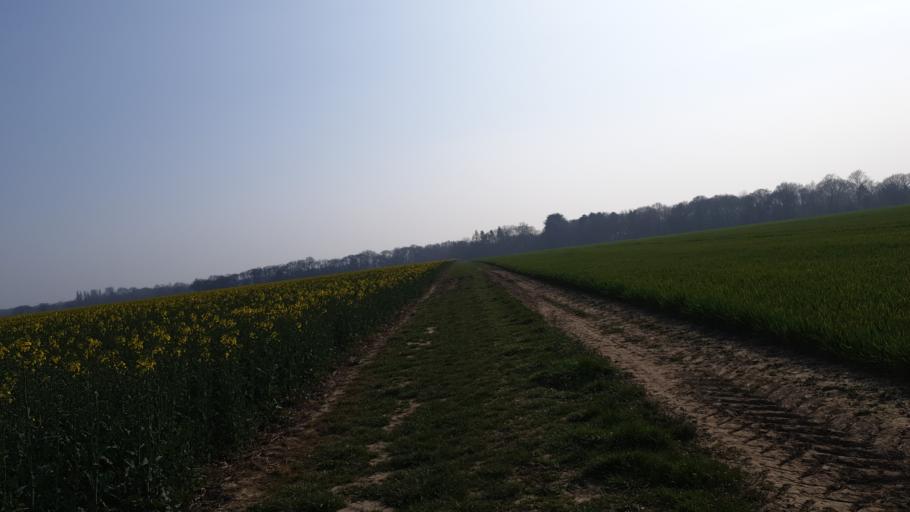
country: GB
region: England
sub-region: Essex
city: Mistley
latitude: 51.8895
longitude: 1.1210
